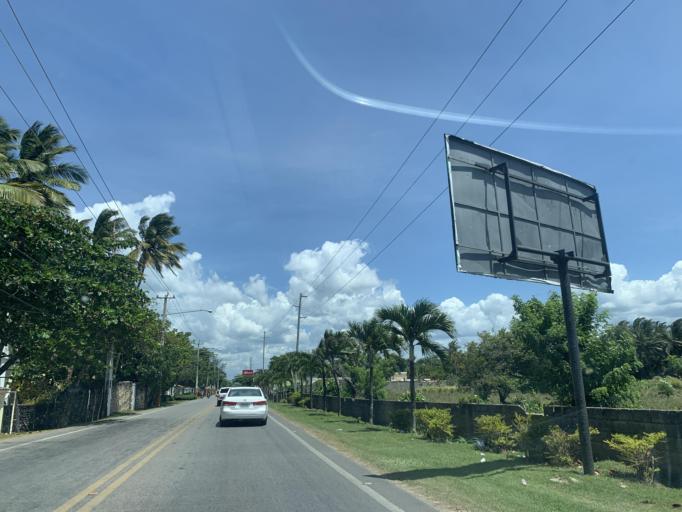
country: DO
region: Puerto Plata
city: Cabarete
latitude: 19.7450
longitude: -70.3948
